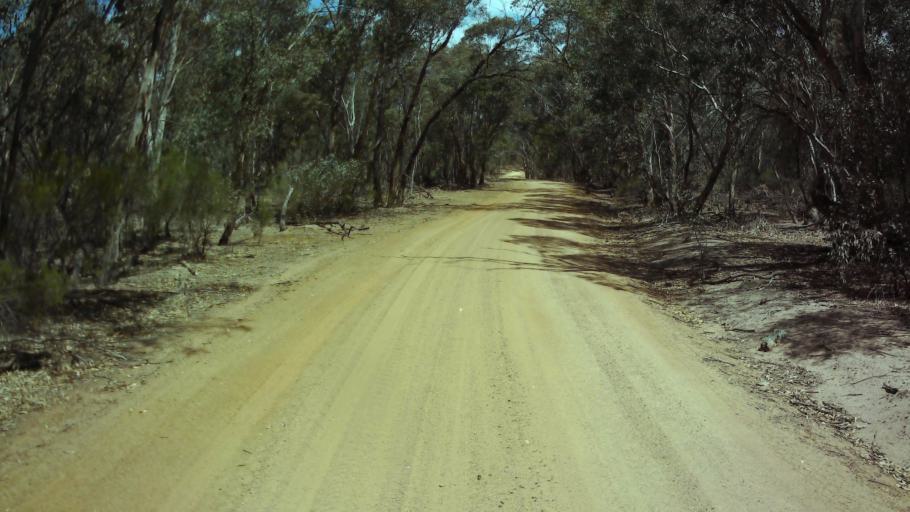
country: AU
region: New South Wales
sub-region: Weddin
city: Grenfell
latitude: -33.8027
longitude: 148.1601
